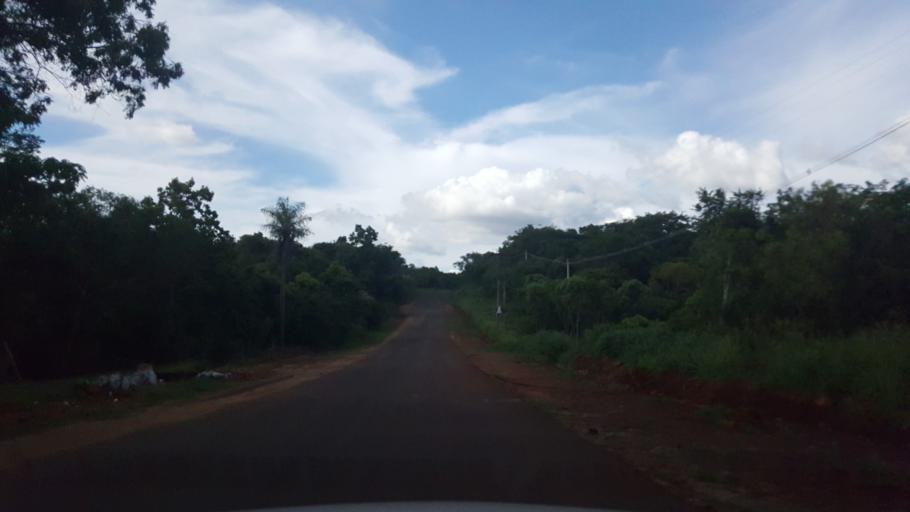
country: AR
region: Misiones
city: Santa Ana
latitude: -27.3606
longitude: -55.5874
